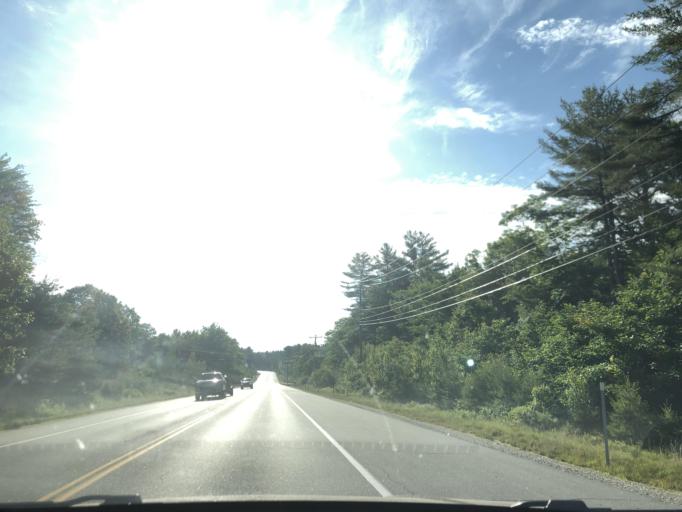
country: US
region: New Hampshire
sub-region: Merrimack County
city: New London
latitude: 43.3937
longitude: -71.9761
